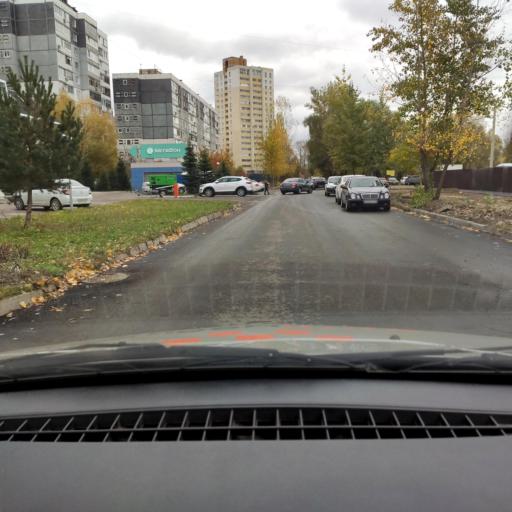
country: RU
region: Bashkortostan
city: Ufa
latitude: 54.7669
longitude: 56.0745
